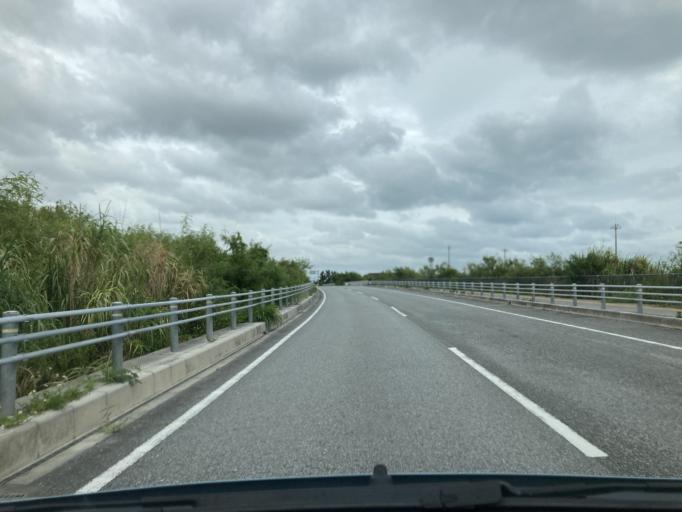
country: JP
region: Okinawa
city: Ginowan
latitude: 26.2150
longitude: 127.7717
